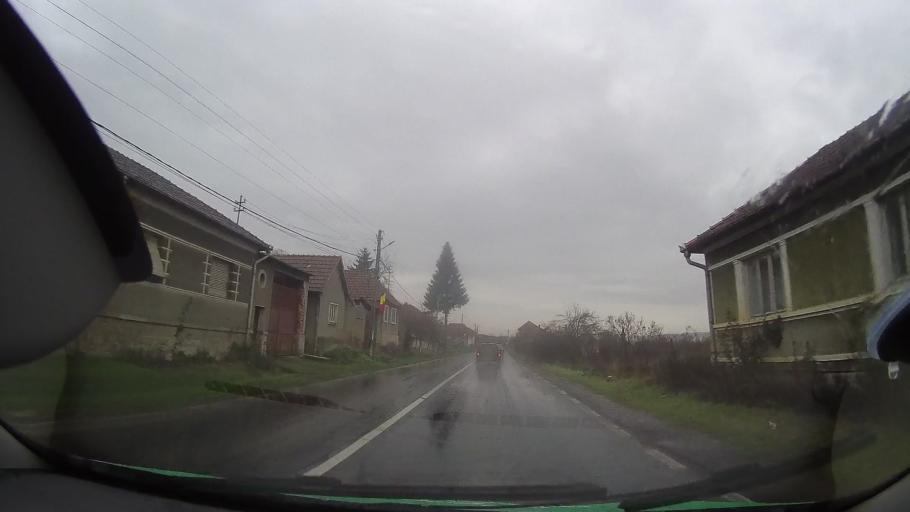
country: RO
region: Bihor
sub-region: Comuna Sambata
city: Sambata
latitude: 46.7611
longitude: 22.1920
